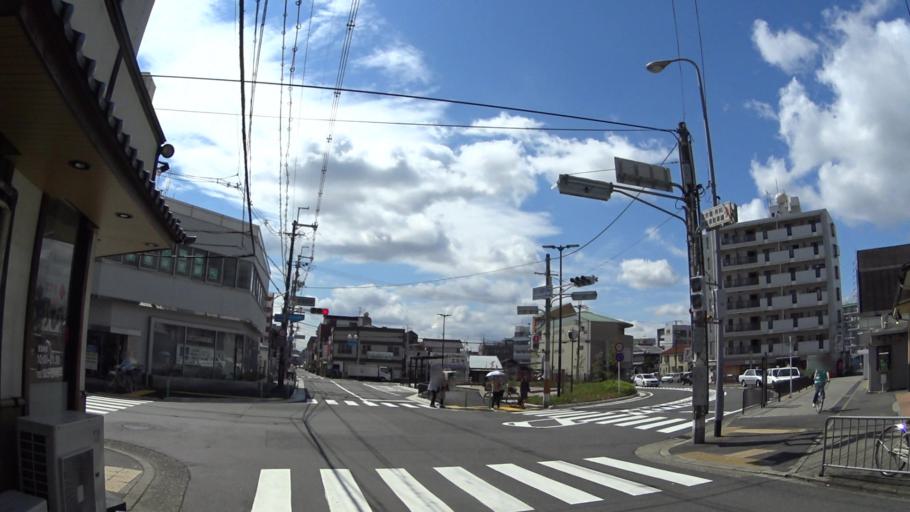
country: JP
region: Kyoto
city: Muko
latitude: 34.9925
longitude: 135.7184
